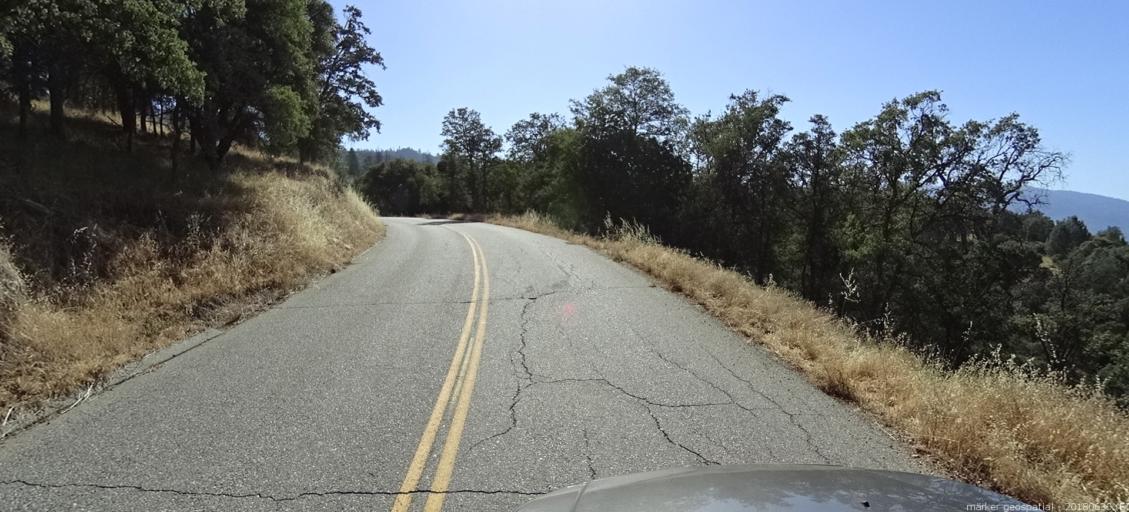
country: US
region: California
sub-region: Fresno County
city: Auberry
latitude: 37.1858
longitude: -119.4229
